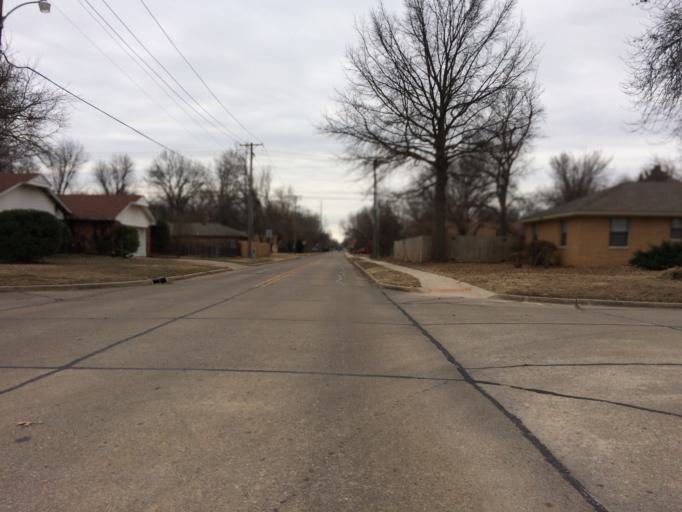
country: US
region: Oklahoma
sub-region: Cleveland County
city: Norman
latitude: 35.2172
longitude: -97.4634
